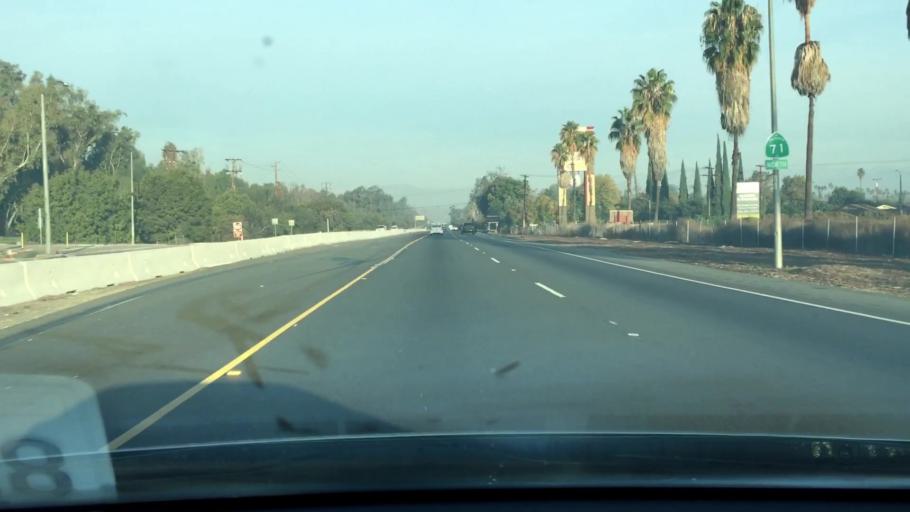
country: US
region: California
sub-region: Los Angeles County
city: Pomona
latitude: 34.0353
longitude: -117.7619
